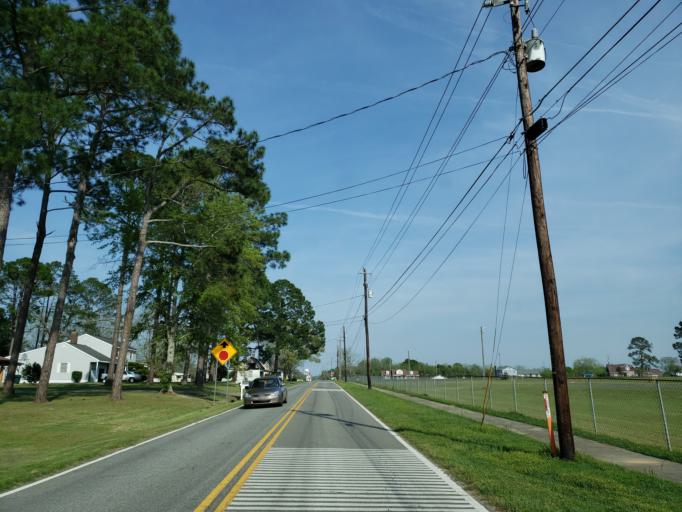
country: US
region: Georgia
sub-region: Dooly County
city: Vienna
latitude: 32.0950
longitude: -83.7844
